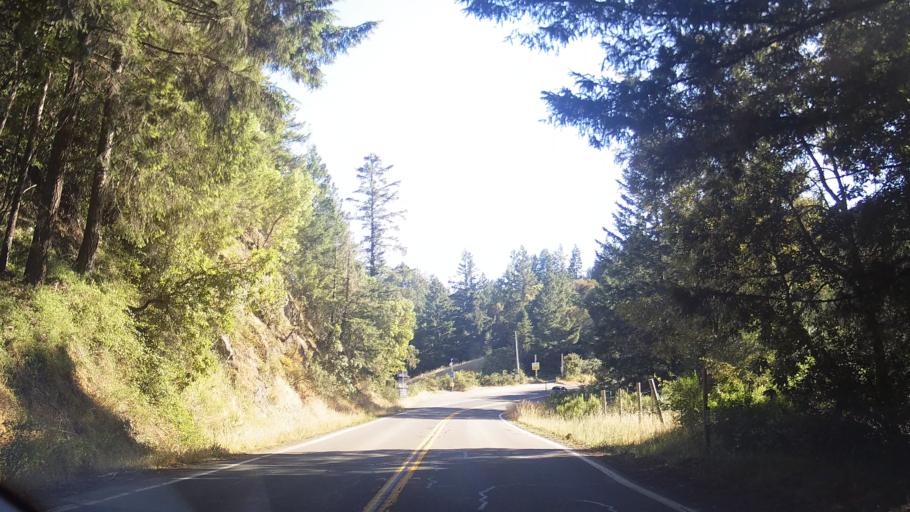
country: US
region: California
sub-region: Mendocino County
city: Brooktrails
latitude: 39.3951
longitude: -123.4547
